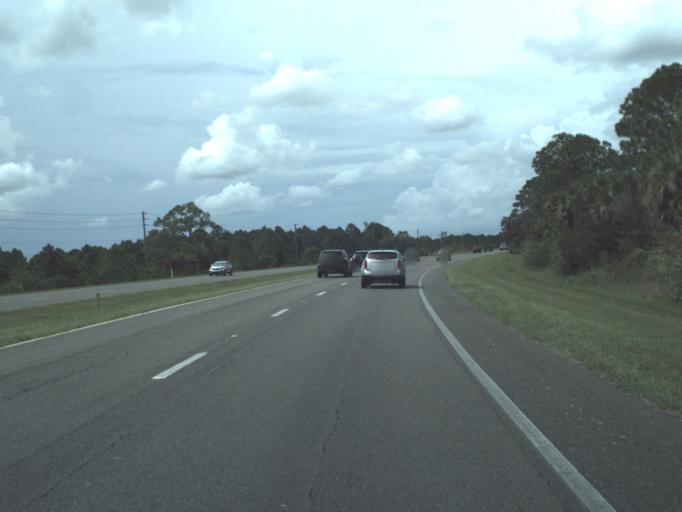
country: US
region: Florida
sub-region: Sarasota County
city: Warm Mineral Springs
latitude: 27.0424
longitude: -82.3051
